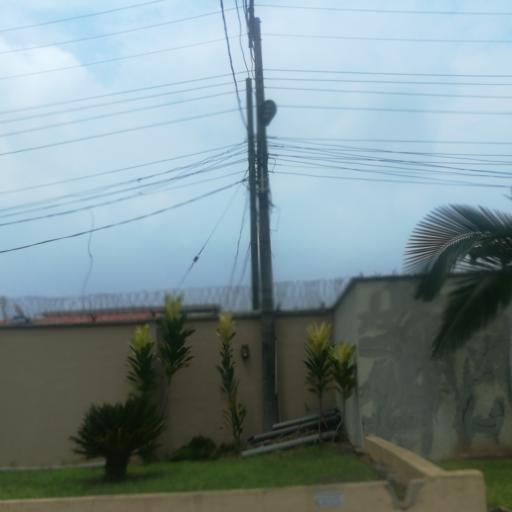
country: NG
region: Lagos
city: Ojota
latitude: 6.5776
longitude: 3.3868
